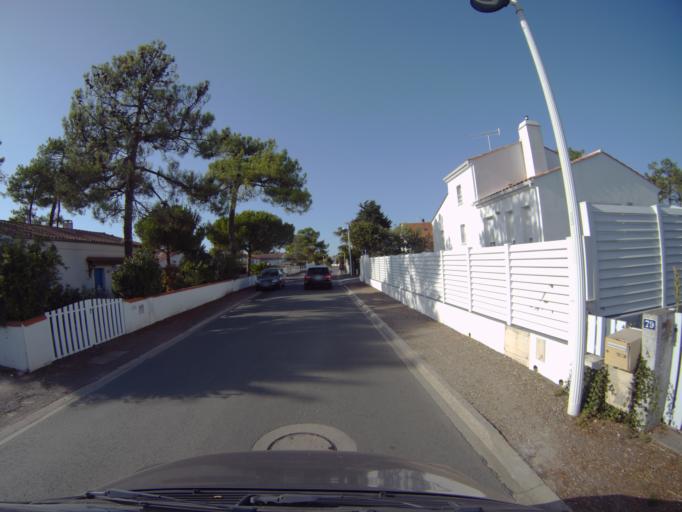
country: FR
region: Pays de la Loire
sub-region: Departement de la Vendee
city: Angles
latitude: 46.3275
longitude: -1.3182
